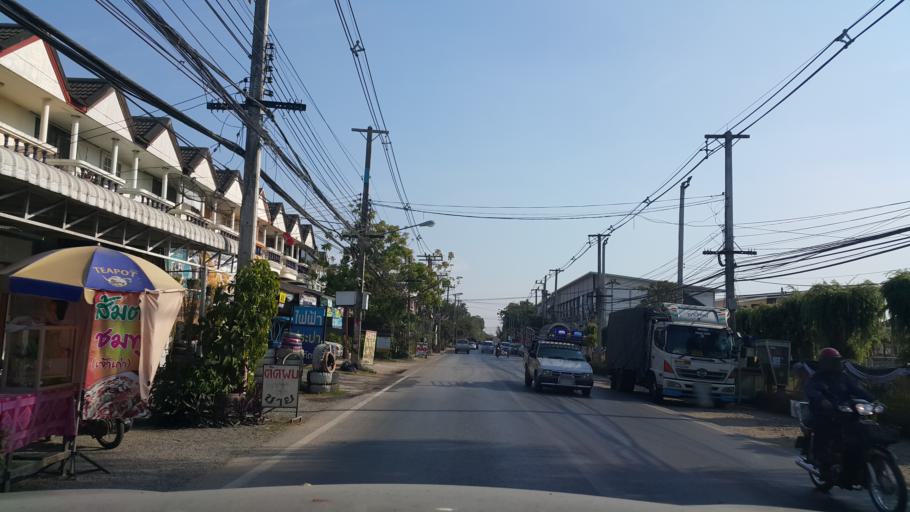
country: TH
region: Chiang Mai
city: San Sai
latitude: 18.8463
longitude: 99.0437
